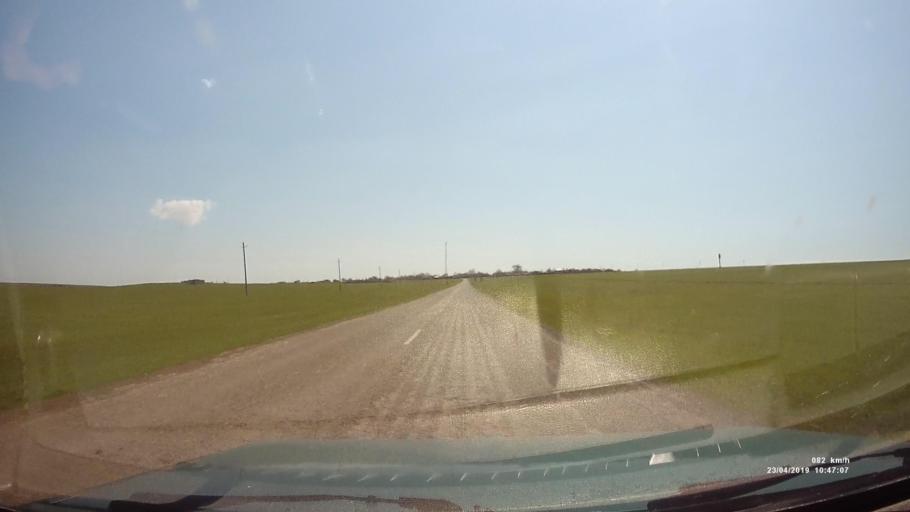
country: RU
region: Kalmykiya
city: Yashalta
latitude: 46.4376
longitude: 42.7020
